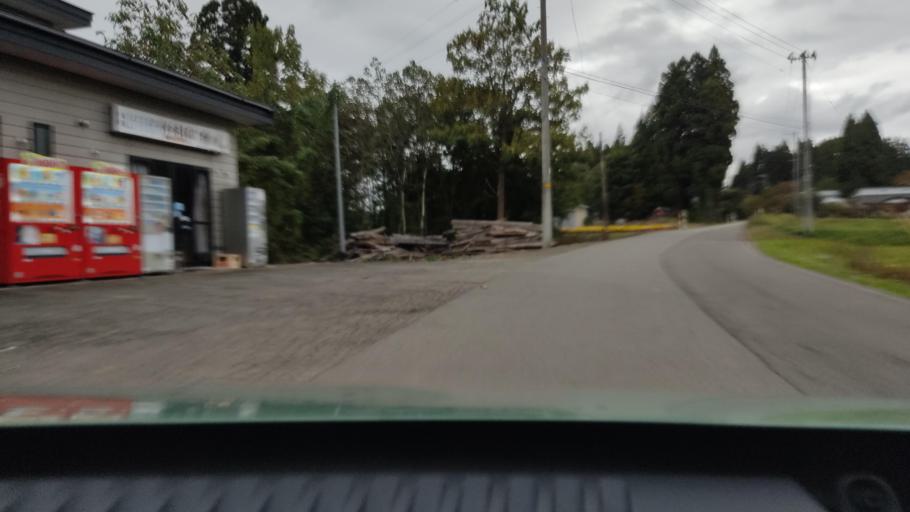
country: JP
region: Akita
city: Kakunodatemachi
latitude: 39.5719
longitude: 140.6134
